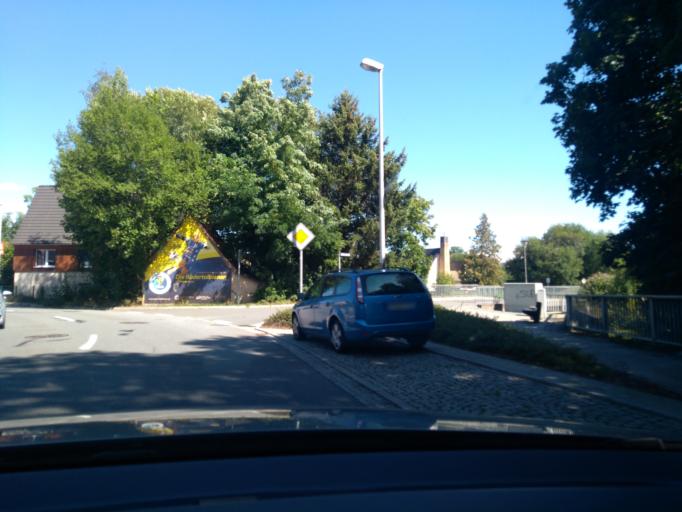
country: DE
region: Saxony
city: Grossrohrsdorf
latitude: 51.1391
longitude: 14.0027
